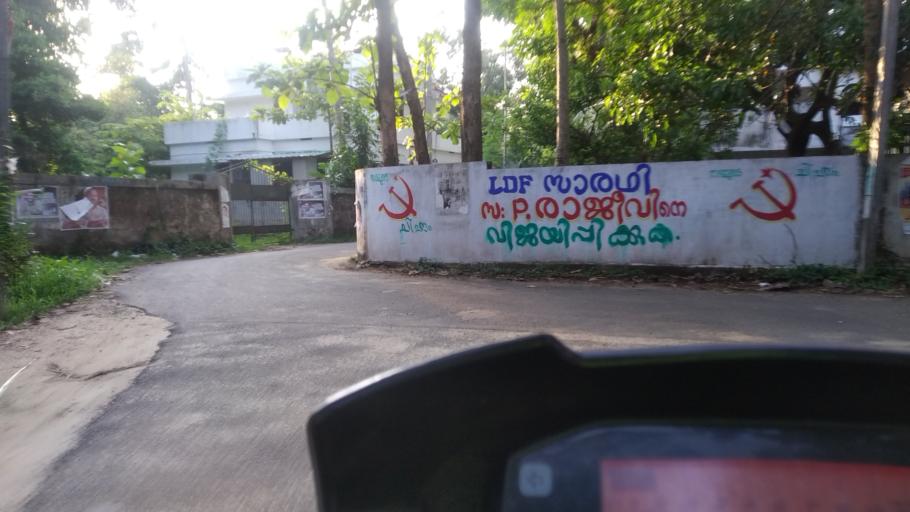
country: IN
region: Kerala
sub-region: Ernakulam
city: Elur
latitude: 10.0686
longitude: 76.2145
